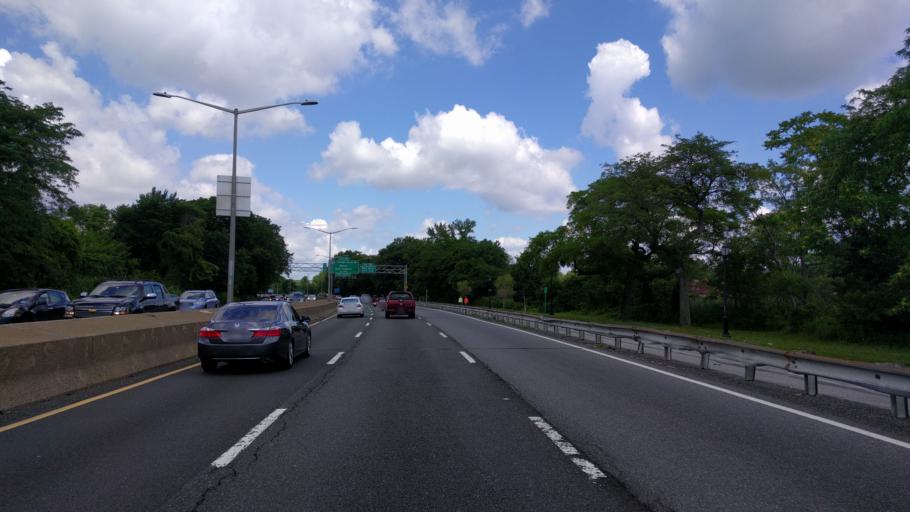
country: US
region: New York
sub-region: Nassau County
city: East Atlantic Beach
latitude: 40.7862
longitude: -73.7748
